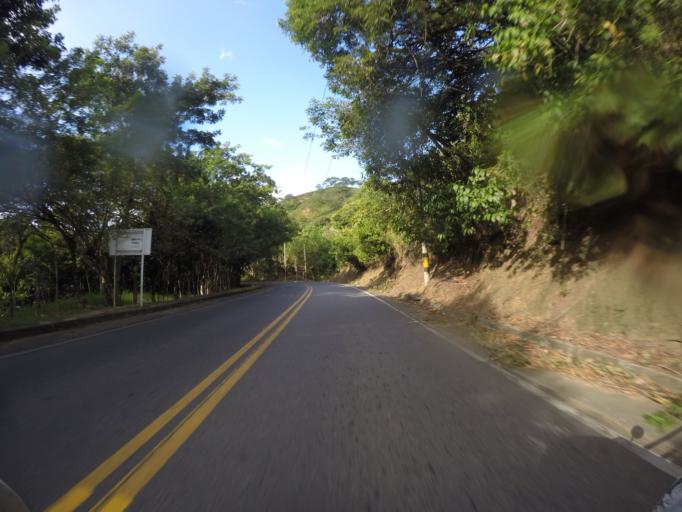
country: CO
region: Valle del Cauca
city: Cartago
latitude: 4.7263
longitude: -75.8722
